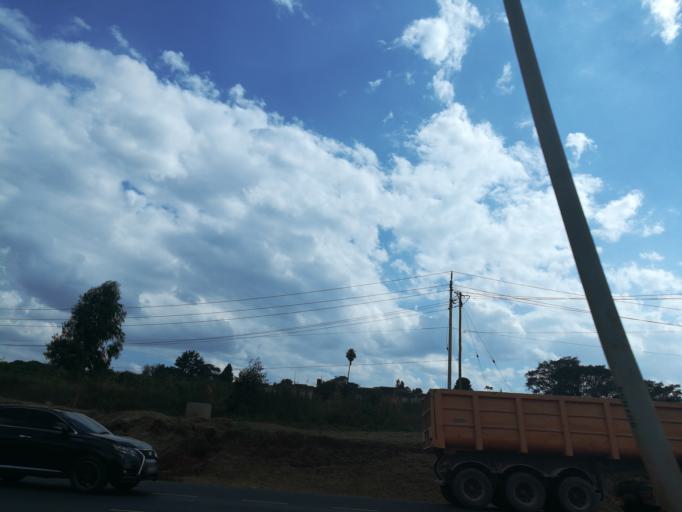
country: KE
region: Nairobi Area
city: Nairobi
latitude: -1.3225
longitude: 36.7921
